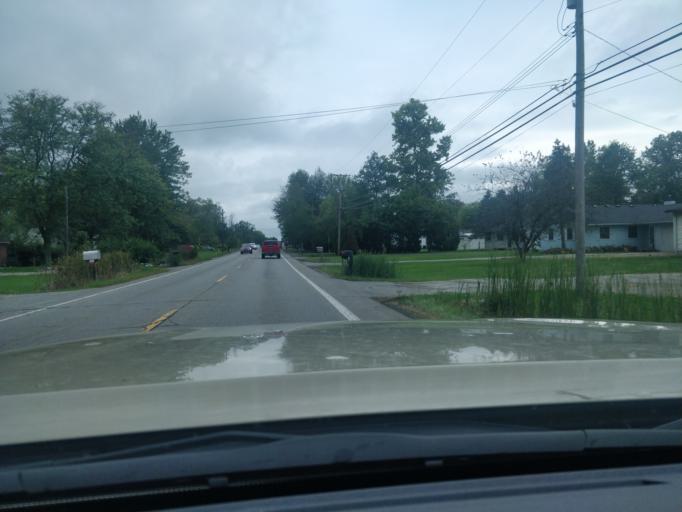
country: US
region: Michigan
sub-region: Wayne County
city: Woodhaven
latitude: 42.1668
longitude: -83.2962
